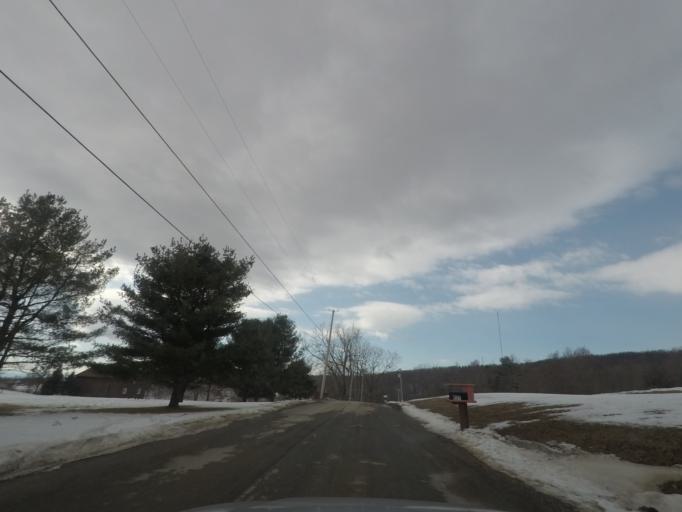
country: US
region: New York
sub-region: Saratoga County
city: Waterford
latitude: 42.7822
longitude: -73.6153
